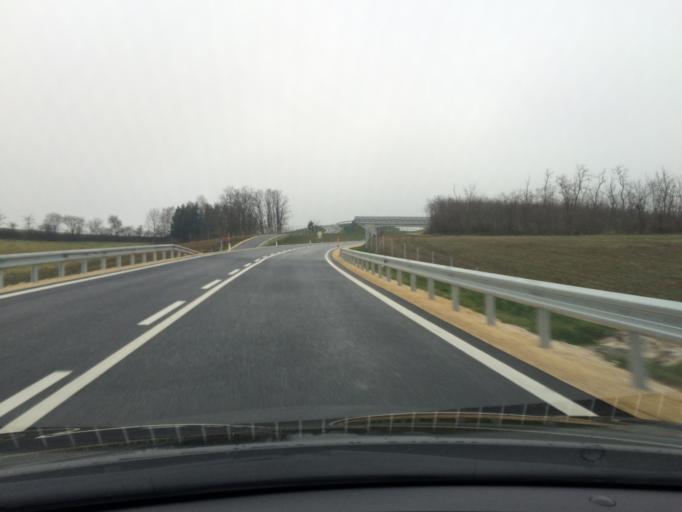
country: AT
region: Lower Austria
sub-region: Politischer Bezirk Mistelbach
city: Wilfersdorf
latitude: 48.5560
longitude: 16.6150
